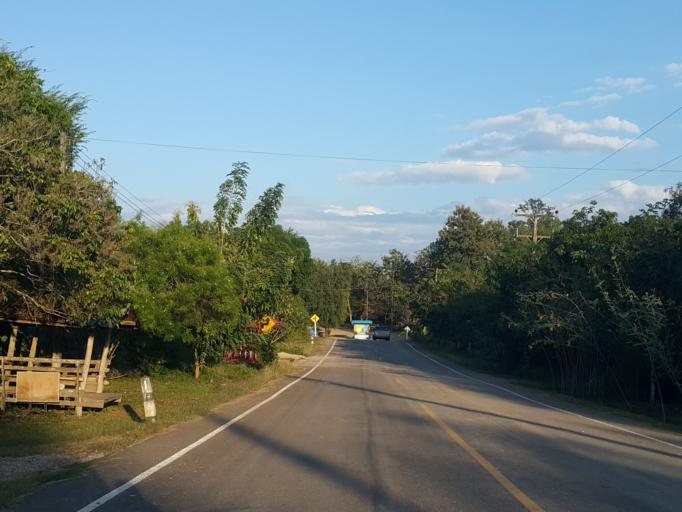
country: TH
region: Lampang
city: Lampang
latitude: 18.4382
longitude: 99.5699
